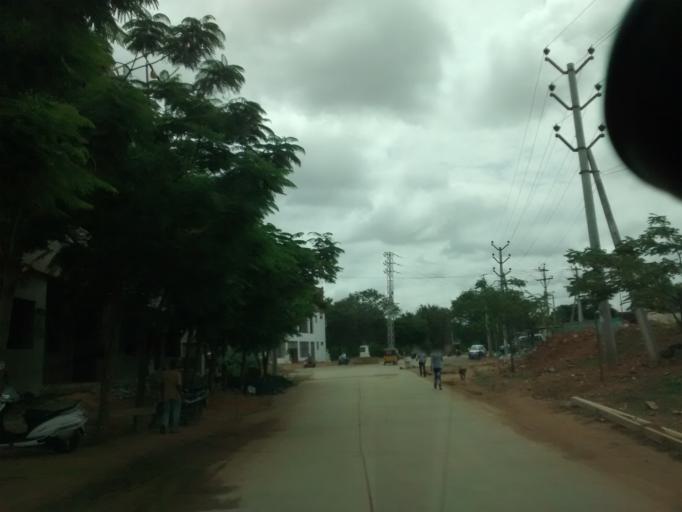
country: IN
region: Andhra Pradesh
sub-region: Anantapur
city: Hindupur
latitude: 13.8239
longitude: 77.4973
